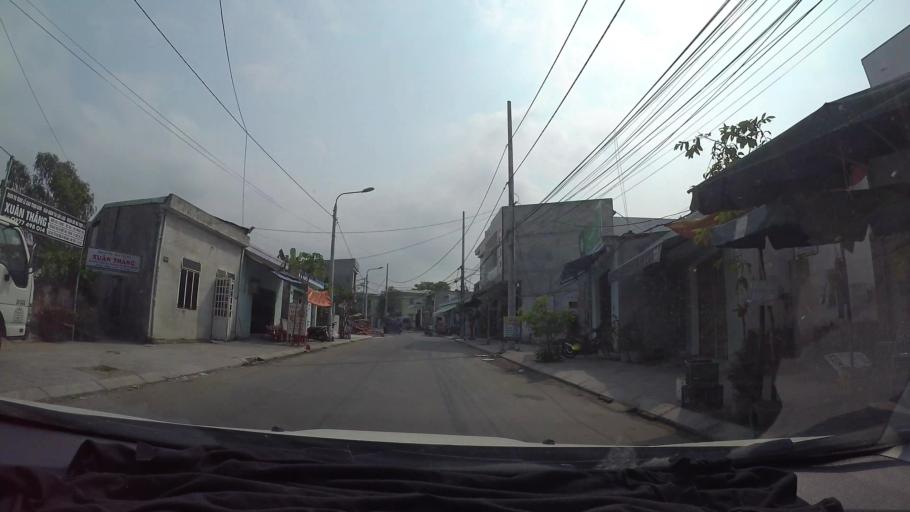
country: VN
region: Da Nang
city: Lien Chieu
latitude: 16.0552
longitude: 108.1565
